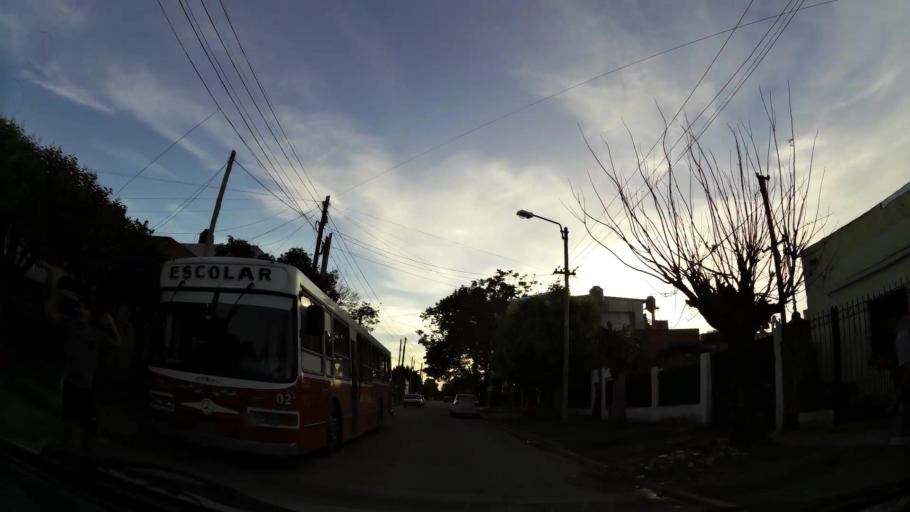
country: AR
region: Buenos Aires
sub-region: Partido de Quilmes
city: Quilmes
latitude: -34.7771
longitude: -58.2030
